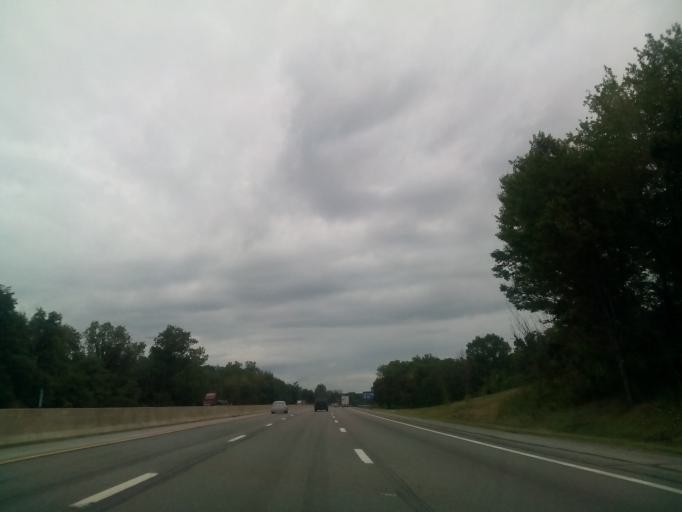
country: US
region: Ohio
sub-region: Lorain County
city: Vermilion
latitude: 41.3433
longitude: -82.3447
